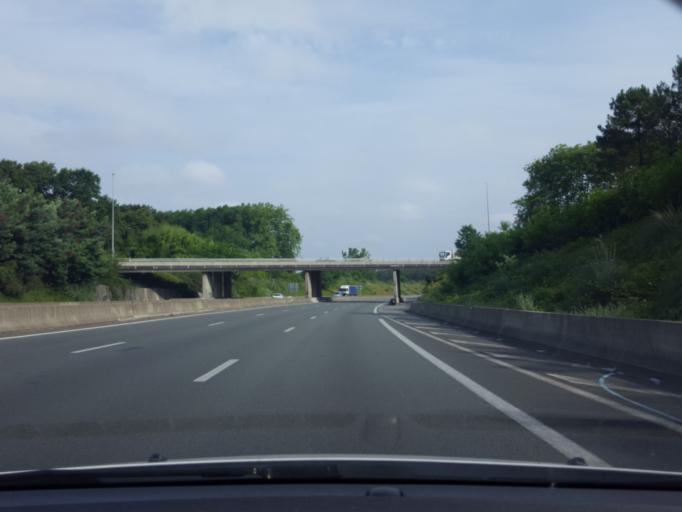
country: FR
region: Aquitaine
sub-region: Departement des Pyrenees-Atlantiques
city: Boucau
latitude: 43.5090
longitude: -1.4424
